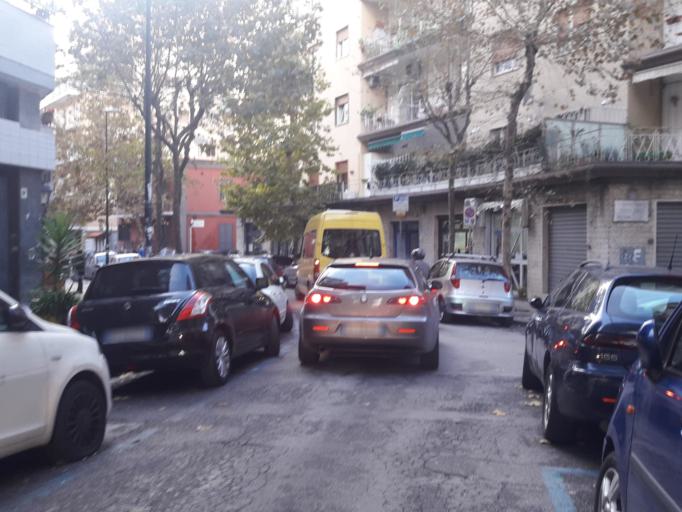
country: IT
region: Campania
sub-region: Provincia di Napoli
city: Napoli
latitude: 40.8462
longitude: 14.2347
